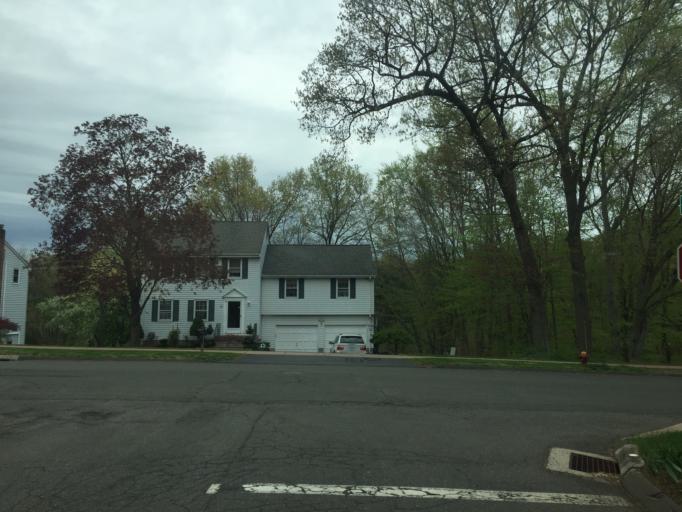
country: US
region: Connecticut
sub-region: Hartford County
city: Glastonbury
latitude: 41.7293
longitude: -72.5945
